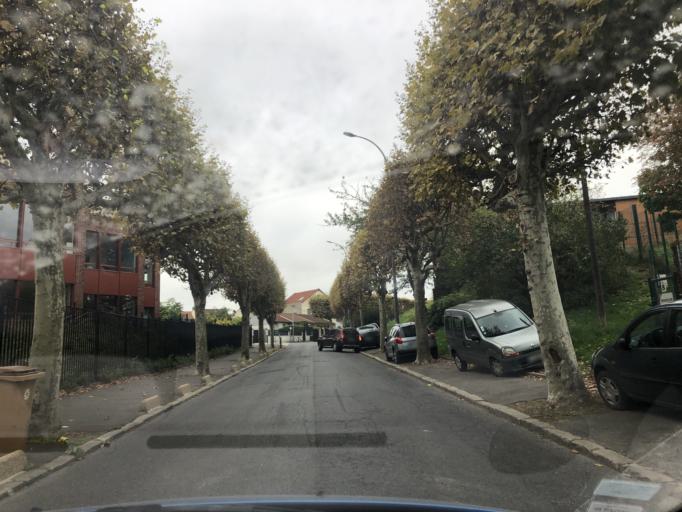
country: FR
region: Ile-de-France
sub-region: Departement du Val-de-Marne
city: Ivry-sur-Seine
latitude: 48.7995
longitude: 2.3891
